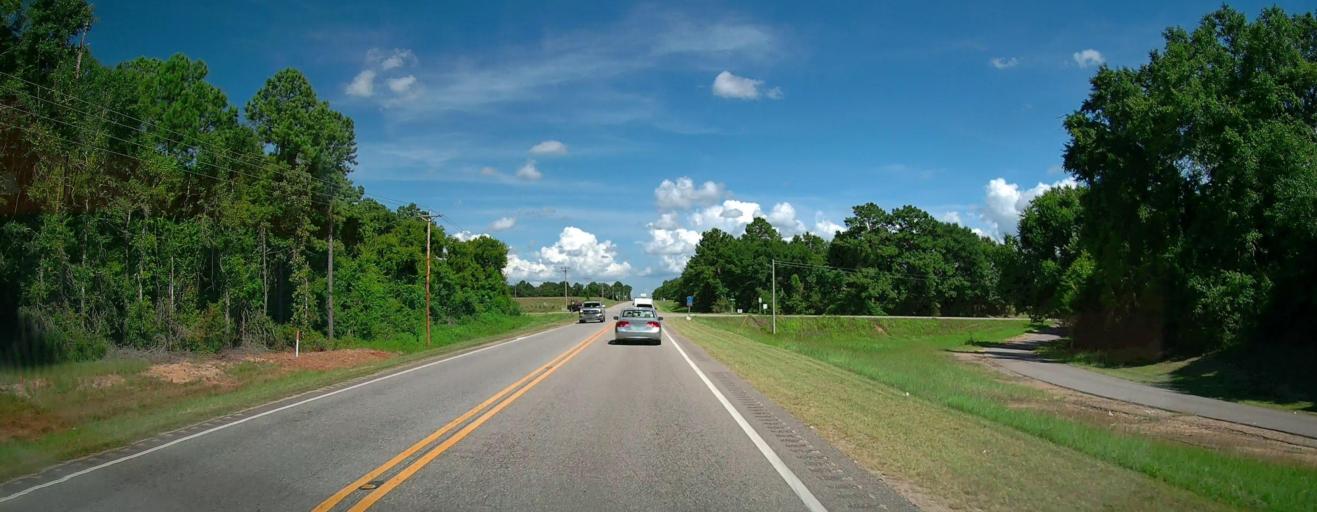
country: US
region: Alabama
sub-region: Elmore County
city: Tallassee
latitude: 32.3957
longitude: -85.9087
